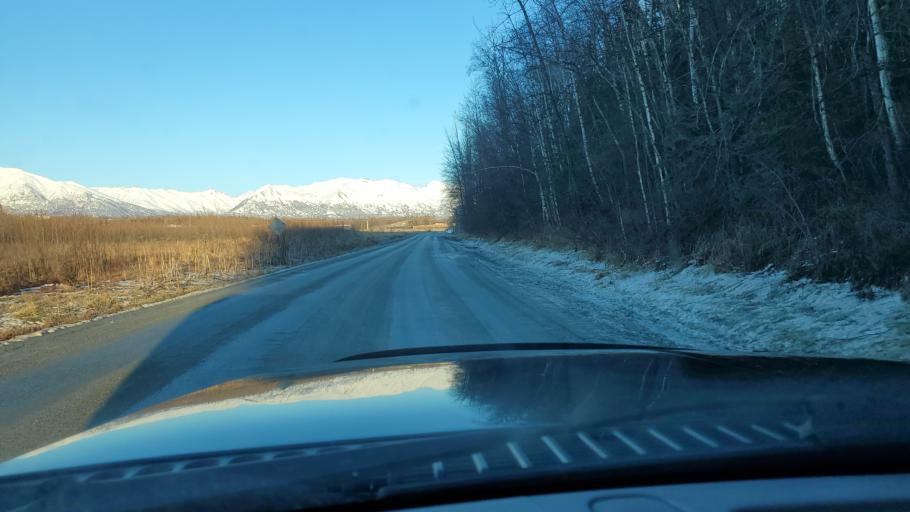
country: US
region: Alaska
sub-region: Matanuska-Susitna Borough
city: Gateway
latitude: 61.5925
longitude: -149.2456
